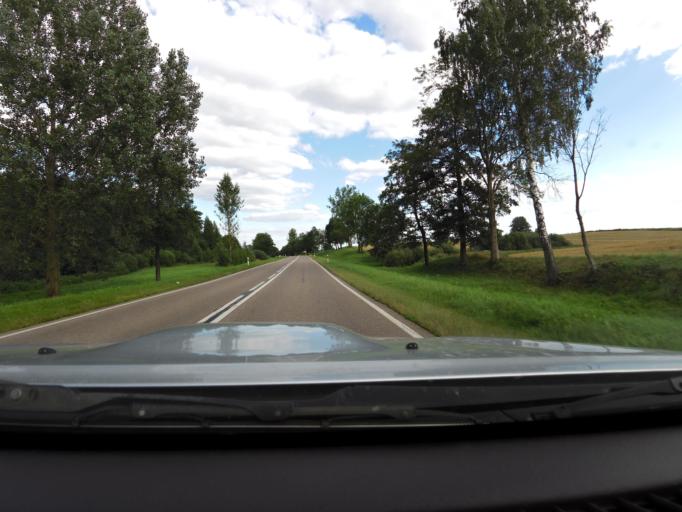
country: PL
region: Podlasie
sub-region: Powiat suwalski
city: Raczki
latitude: 53.8466
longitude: 22.7909
